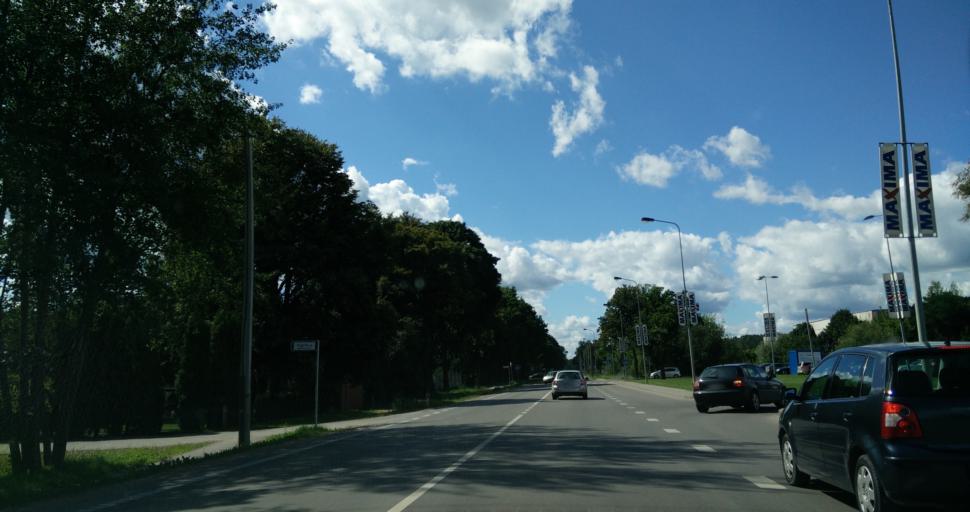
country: LT
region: Kauno apskritis
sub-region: Kauno rajonas
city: Akademija (Kaunas)
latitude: 54.9205
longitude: 23.8219
